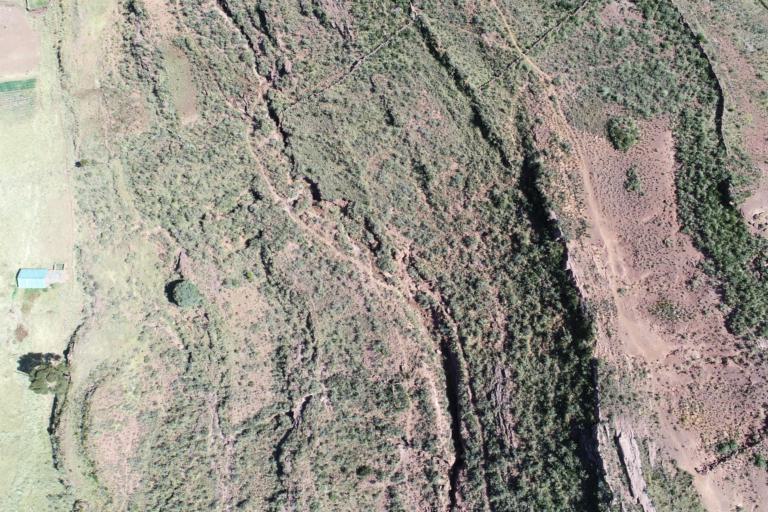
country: BO
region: La Paz
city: Tiahuanaco
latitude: -16.6097
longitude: -68.7685
